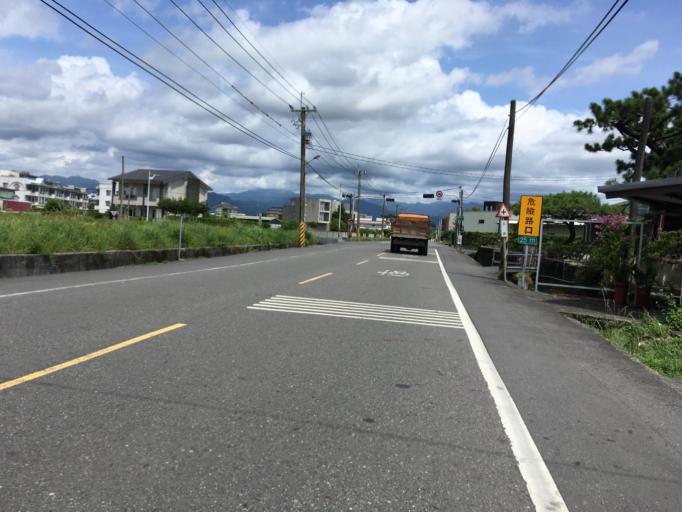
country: TW
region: Taiwan
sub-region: Yilan
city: Yilan
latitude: 24.6987
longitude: 121.7634
